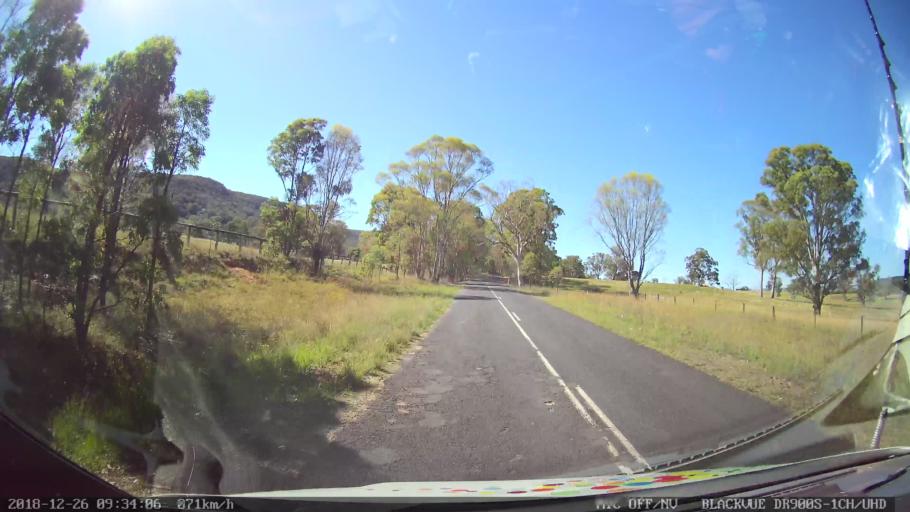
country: AU
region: New South Wales
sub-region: Mid-Western Regional
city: Kandos
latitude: -32.9017
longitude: 150.0371
